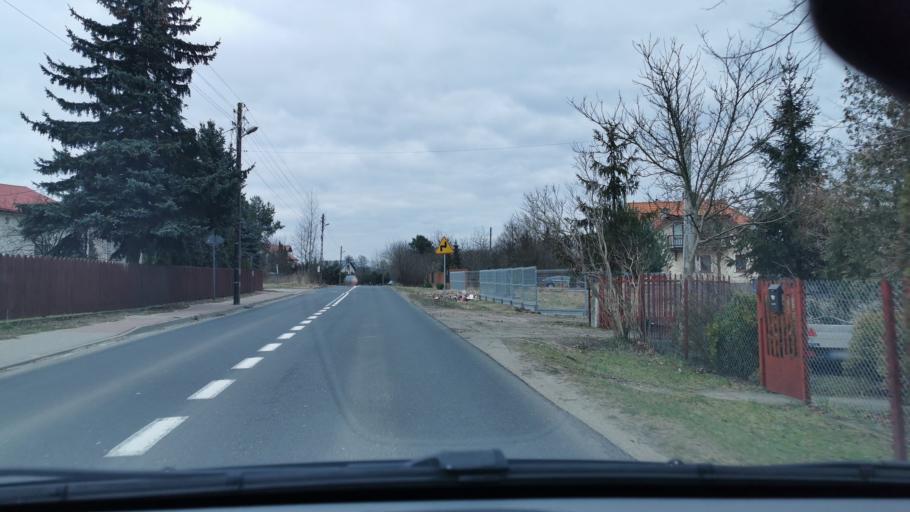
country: PL
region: Masovian Voivodeship
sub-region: Powiat zyrardowski
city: Radziejowice
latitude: 52.0099
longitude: 20.5340
